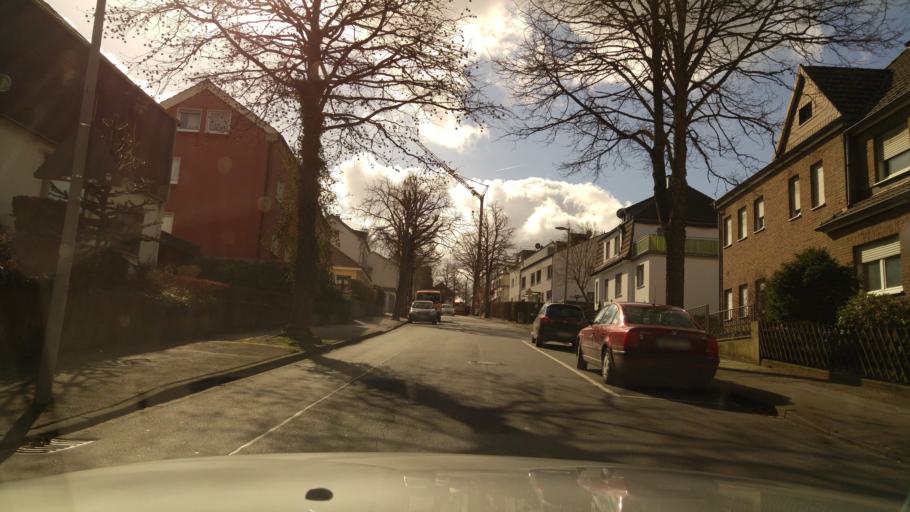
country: DE
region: North Rhine-Westphalia
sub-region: Regierungsbezirk Arnsberg
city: Menden
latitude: 51.4471
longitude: 7.7935
